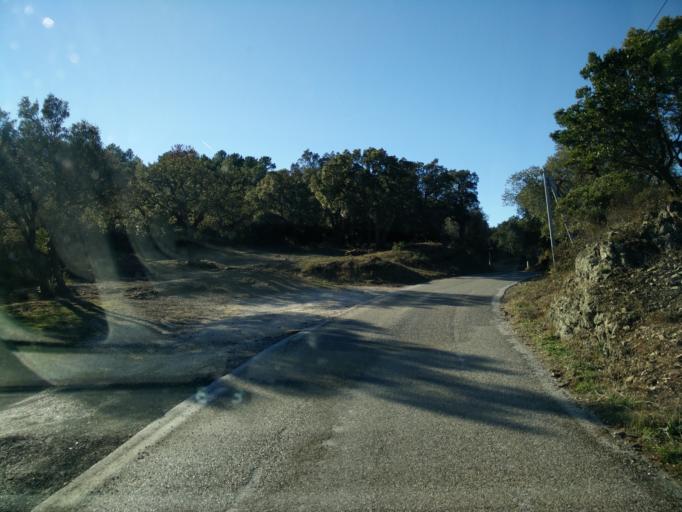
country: FR
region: Provence-Alpes-Cote d'Azur
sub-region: Departement du Var
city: La Garde-Freinet
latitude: 43.2553
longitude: 6.4265
